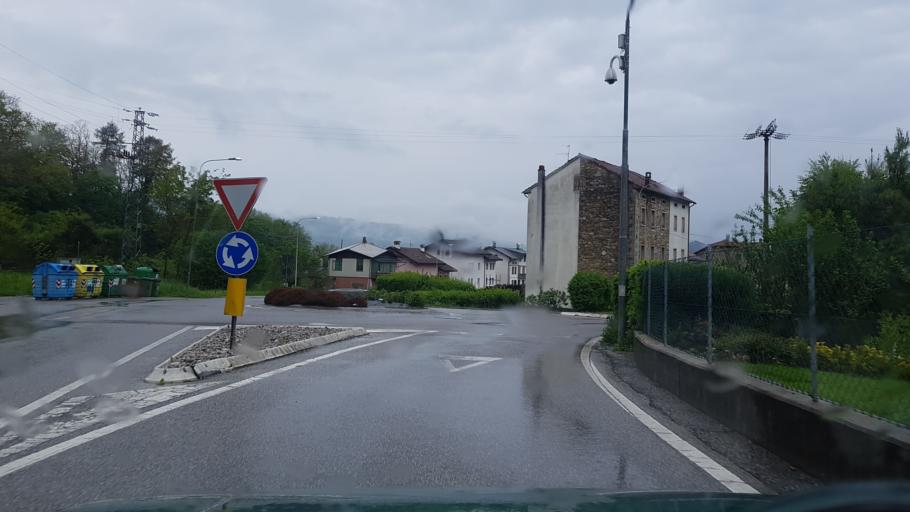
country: IT
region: Veneto
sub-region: Provincia di Belluno
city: Farra d'Alpago
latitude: 46.1175
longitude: 12.3625
